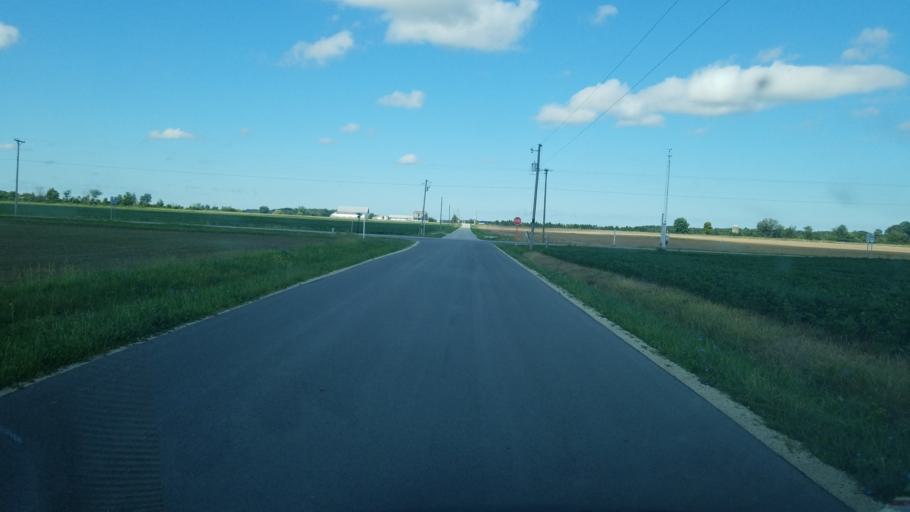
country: US
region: Ohio
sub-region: Seneca County
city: Fostoria
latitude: 41.0648
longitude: -83.4005
